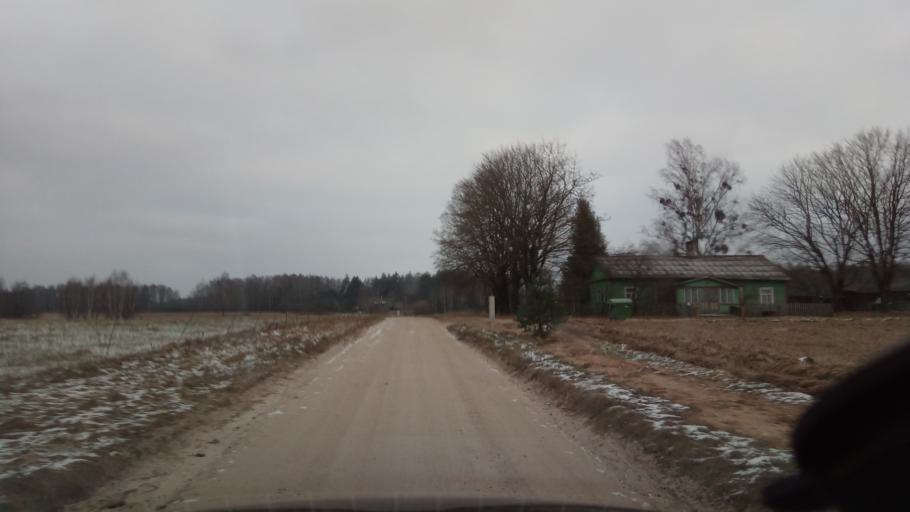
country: LT
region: Alytaus apskritis
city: Varena
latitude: 54.1194
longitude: 24.7047
